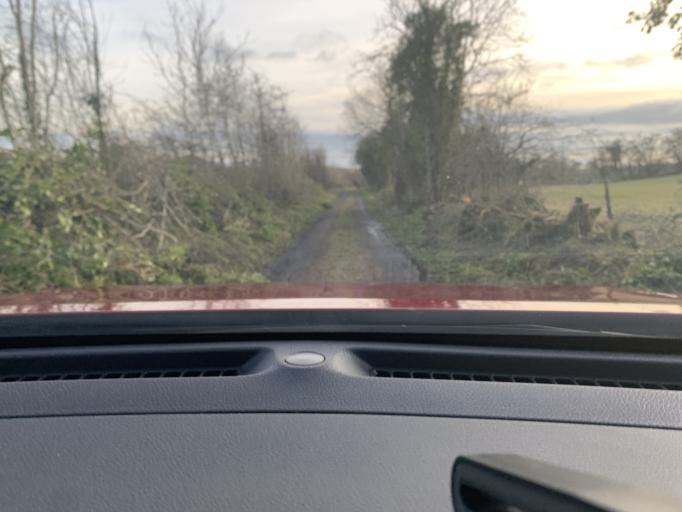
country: IE
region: Connaught
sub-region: Sligo
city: Strandhill
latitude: 54.1713
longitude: -8.6474
